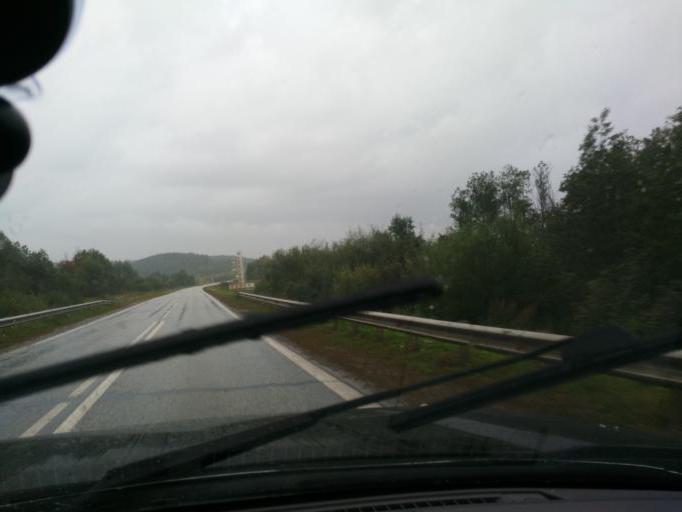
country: RU
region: Perm
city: Osa
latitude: 57.1061
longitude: 55.5251
